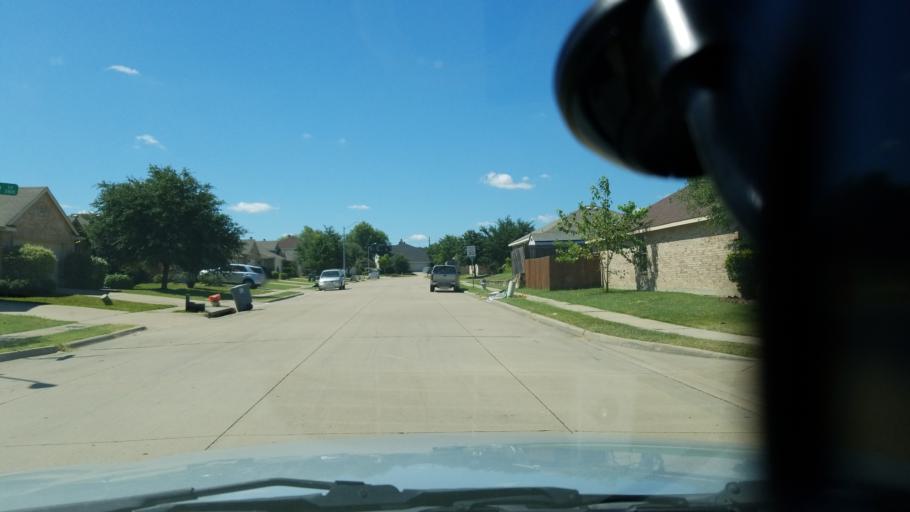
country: US
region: Texas
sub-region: Dallas County
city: Duncanville
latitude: 32.6569
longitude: -96.8648
